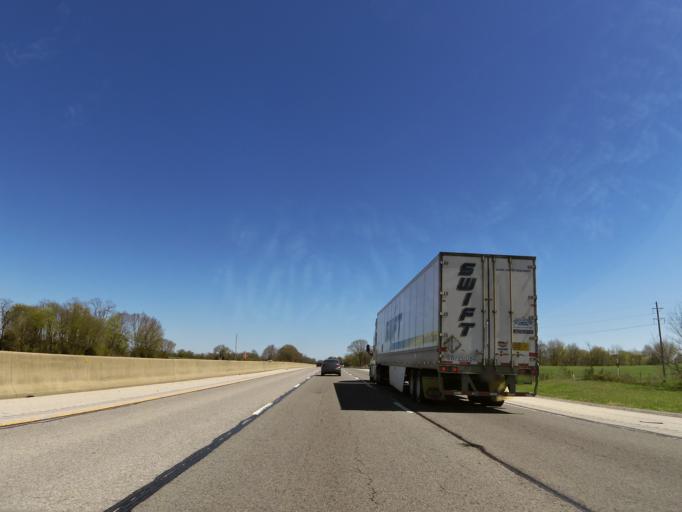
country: US
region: Kentucky
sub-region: Warren County
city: Bowling Green
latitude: 37.0121
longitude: -86.3158
